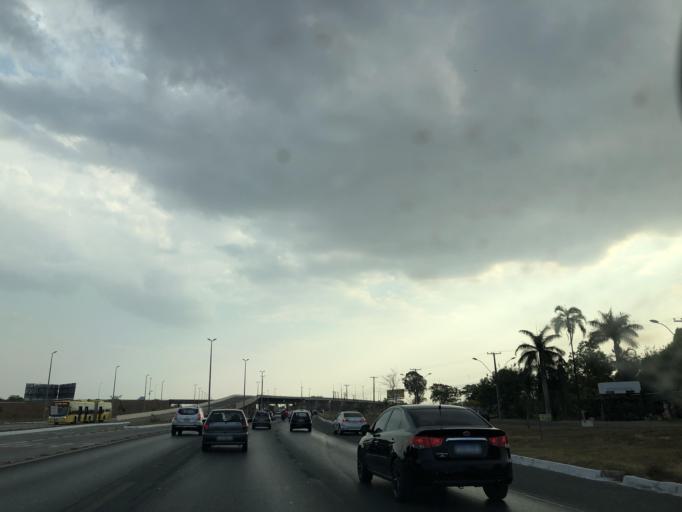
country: BR
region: Federal District
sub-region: Brasilia
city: Brasilia
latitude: -15.9444
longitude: -47.9899
